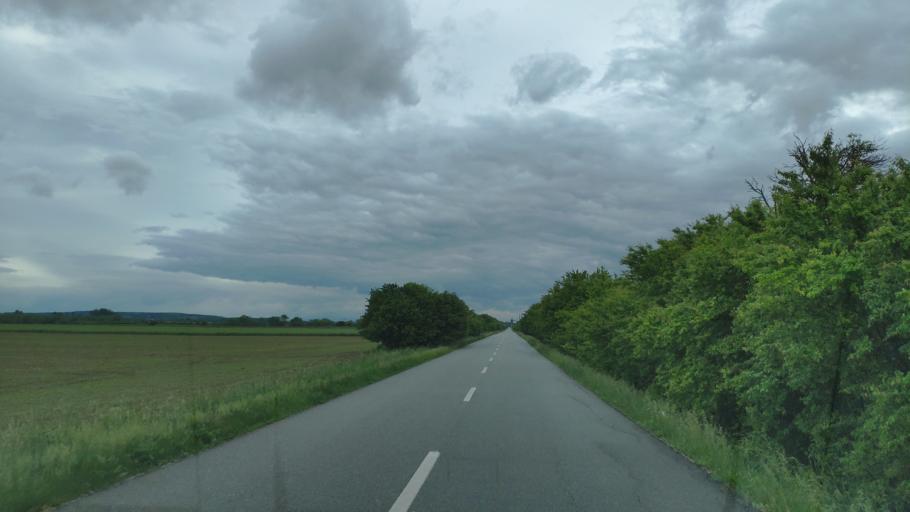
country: SK
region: Kosicky
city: Moldava nad Bodvou
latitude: 48.5823
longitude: 21.1342
